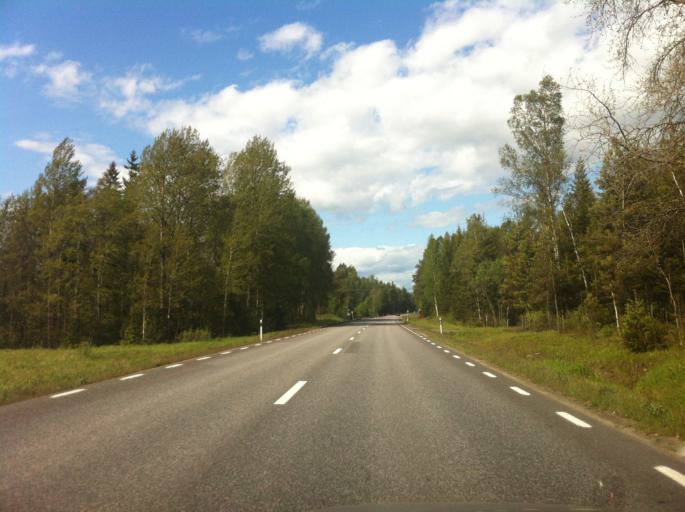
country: SE
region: Vaermland
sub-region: Kristinehamns Kommun
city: Bjorneborg
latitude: 59.1738
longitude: 14.1765
